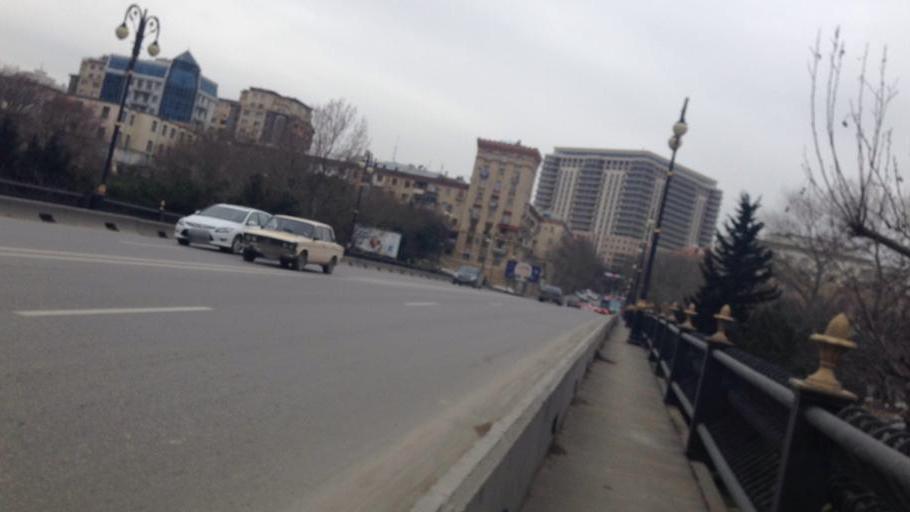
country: AZ
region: Baki
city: Badamdar
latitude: 40.3870
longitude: 49.8291
